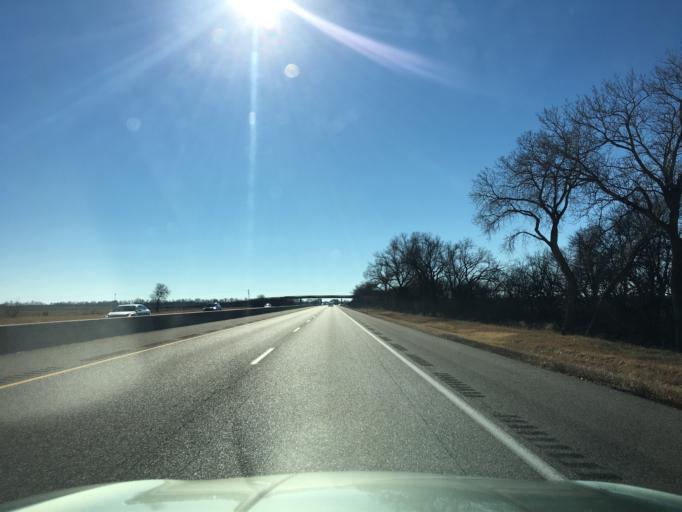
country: US
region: Kansas
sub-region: Sumner County
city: Belle Plaine
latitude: 37.4395
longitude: -97.3217
